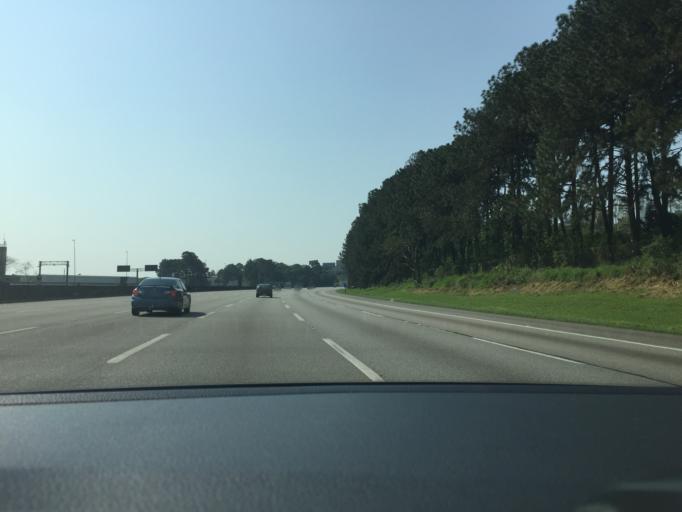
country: BR
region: Sao Paulo
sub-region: Sao Bernardo Do Campo
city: Sao Bernardo do Campo
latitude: -23.7852
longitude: -46.5977
